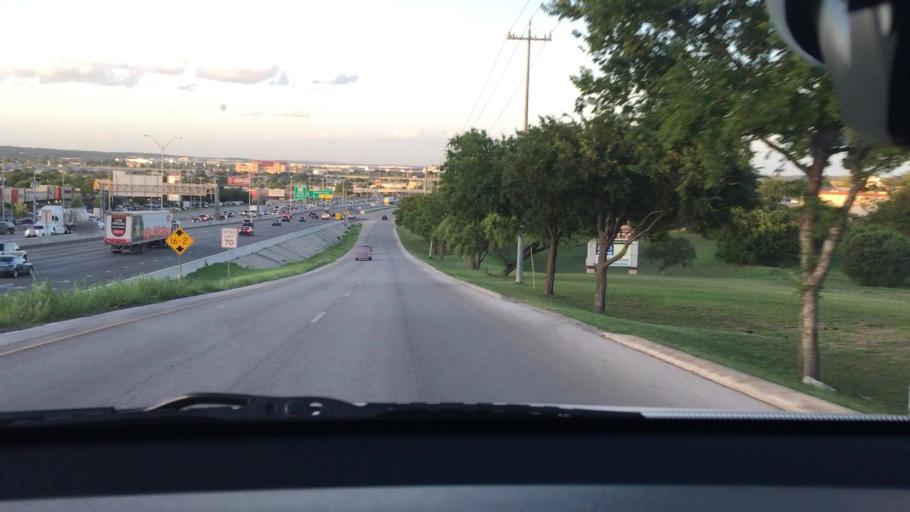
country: US
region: Texas
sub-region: Bexar County
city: Live Oak
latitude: 29.5729
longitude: -98.3269
